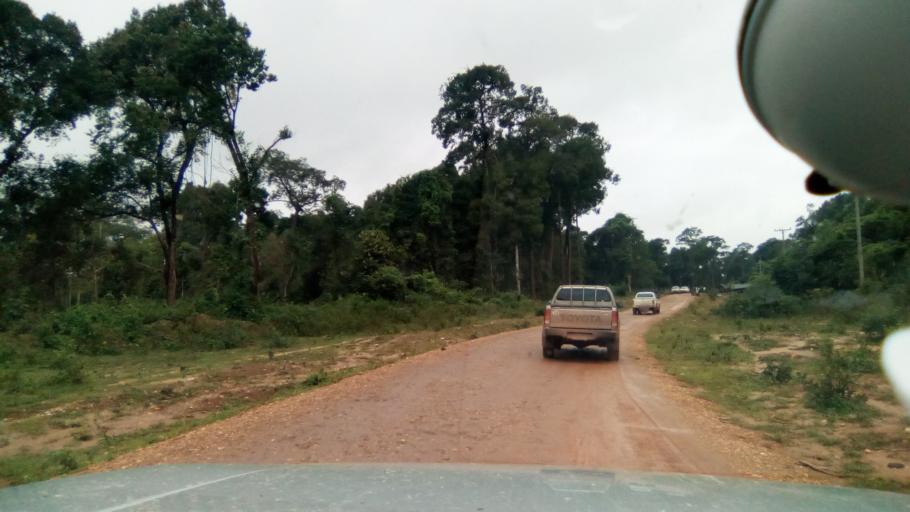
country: LA
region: Attapu
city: Attapu
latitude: 14.6755
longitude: 106.5623
